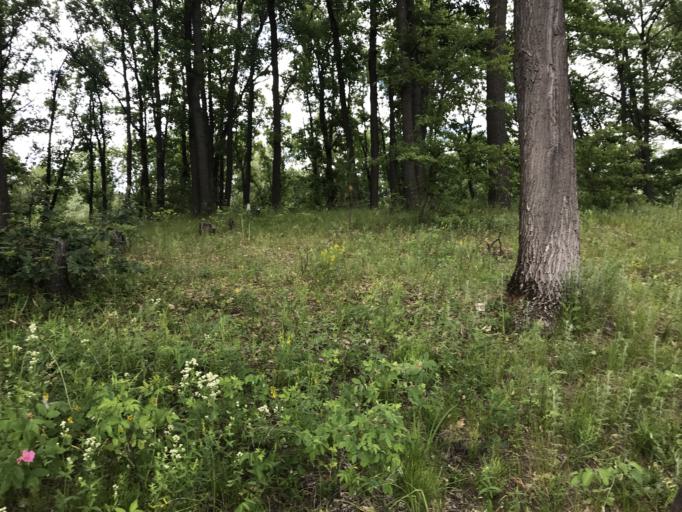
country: RU
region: Samara
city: Pribrezhnyy
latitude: 53.4680
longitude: 49.8167
